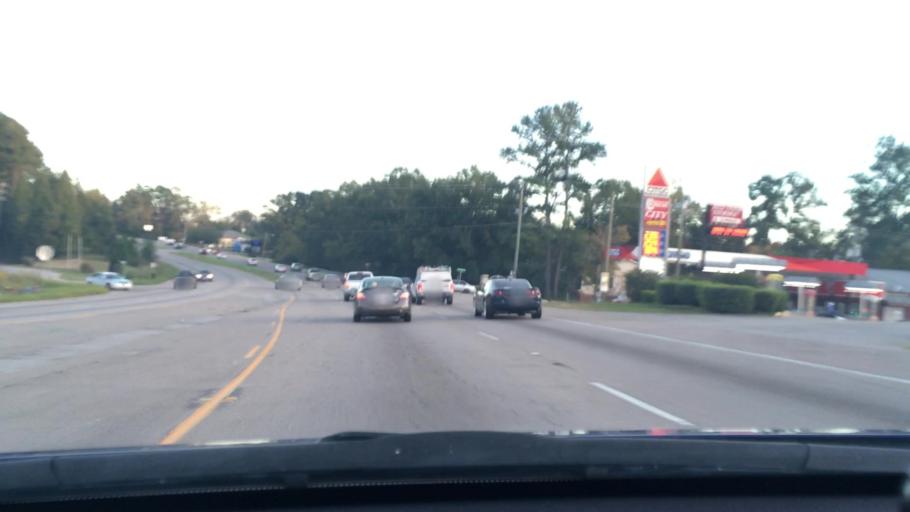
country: US
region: South Carolina
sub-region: Richland County
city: Forest Acres
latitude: 33.9595
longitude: -80.9393
